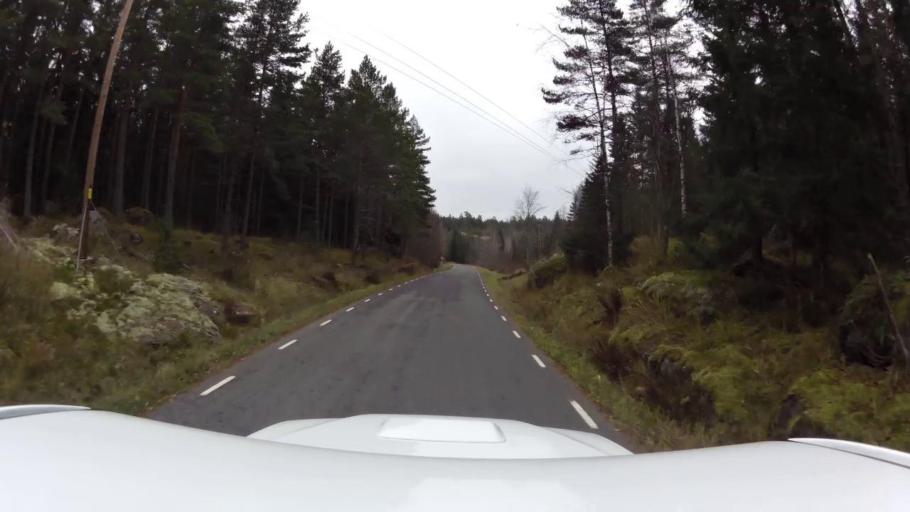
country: SE
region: OEstergoetland
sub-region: Kinda Kommun
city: Rimforsa
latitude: 58.1372
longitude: 15.5897
